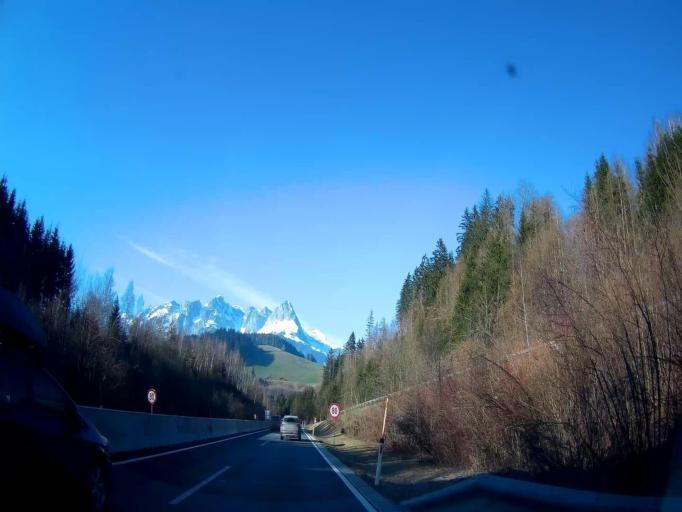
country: AT
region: Salzburg
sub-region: Politischer Bezirk Sankt Johann im Pongau
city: Bischofshofen
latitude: 47.4309
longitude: 13.2247
